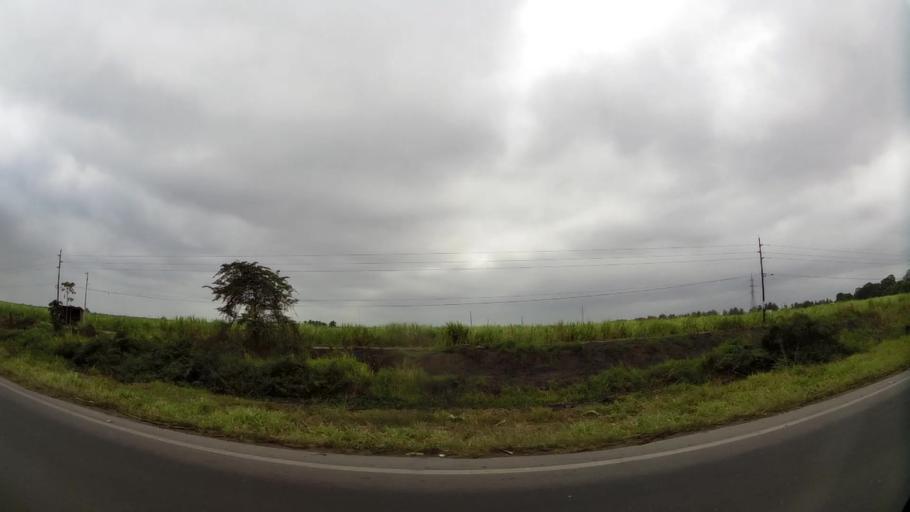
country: EC
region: Guayas
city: Yaguachi Nuevo
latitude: -2.2936
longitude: -79.6393
